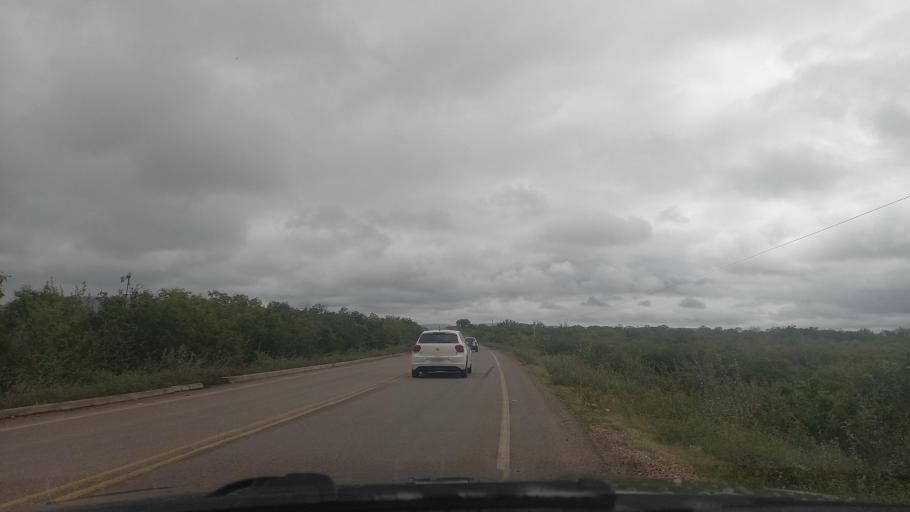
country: BR
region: Bahia
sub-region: Paulo Afonso
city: Paulo Afonso
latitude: -9.3158
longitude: -38.2921
